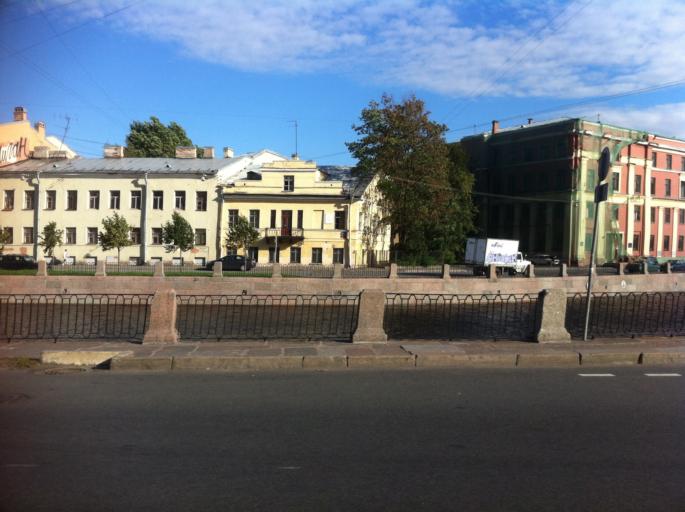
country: RU
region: St.-Petersburg
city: Admiralteisky
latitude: 59.9186
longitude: 30.2817
